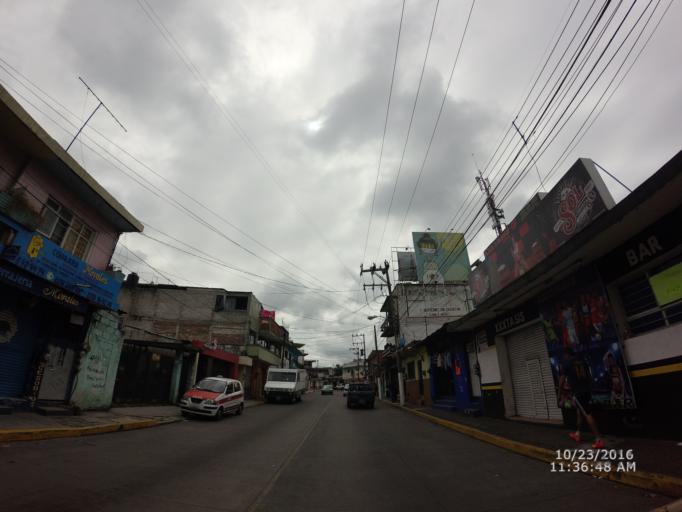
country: MX
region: Veracruz
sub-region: Xalapa
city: Xalapa de Enriquez
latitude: 19.5363
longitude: -96.9303
